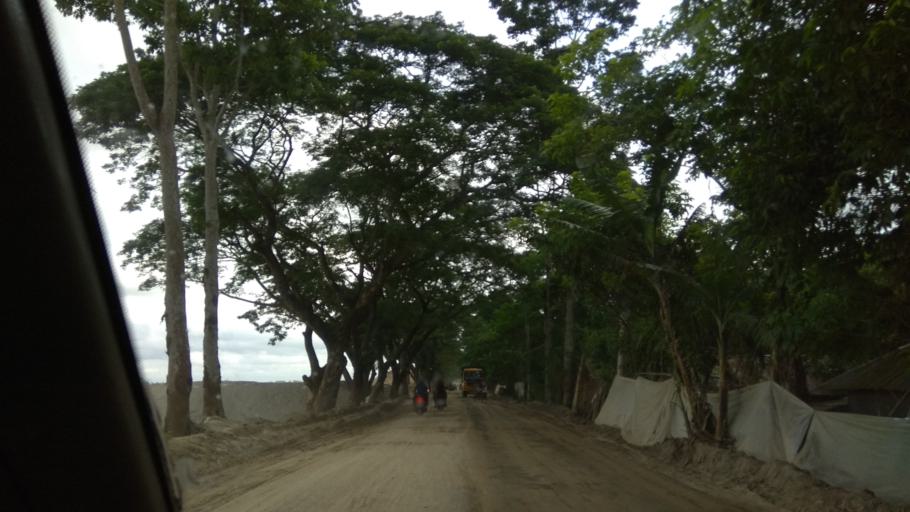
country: BD
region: Khulna
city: Kalia
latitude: 23.1986
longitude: 89.6970
